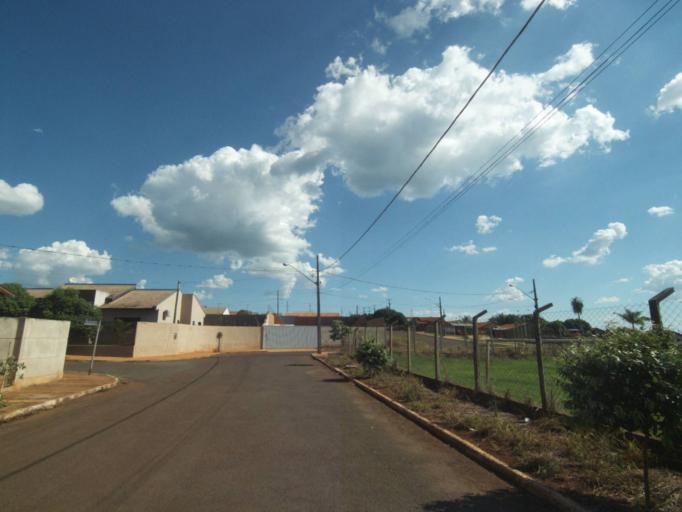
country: BR
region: Parana
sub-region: Sertanopolis
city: Sertanopolis
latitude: -23.0440
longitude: -50.8181
